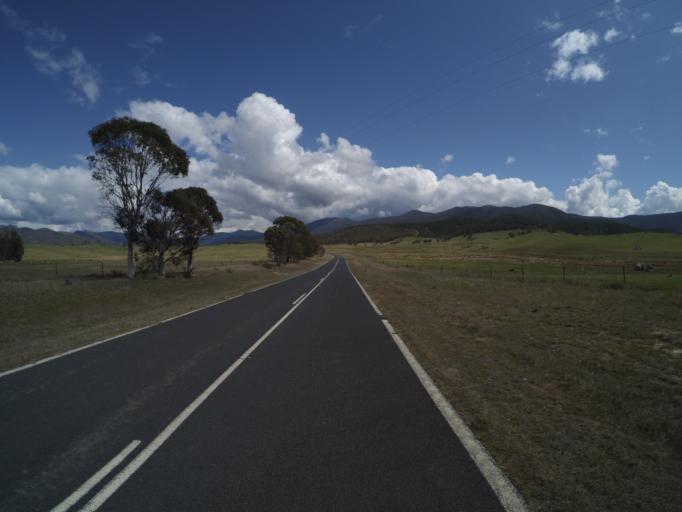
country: AU
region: Australian Capital Territory
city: Macarthur
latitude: -35.4067
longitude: 148.9538
